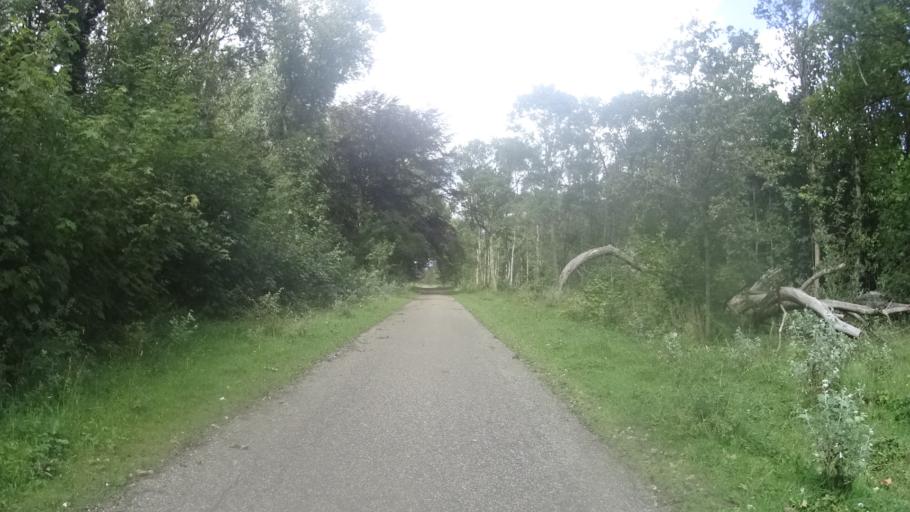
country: NL
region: North Holland
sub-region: Gemeente Bergen
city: Egmond aan Zee
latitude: 52.5793
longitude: 4.6344
